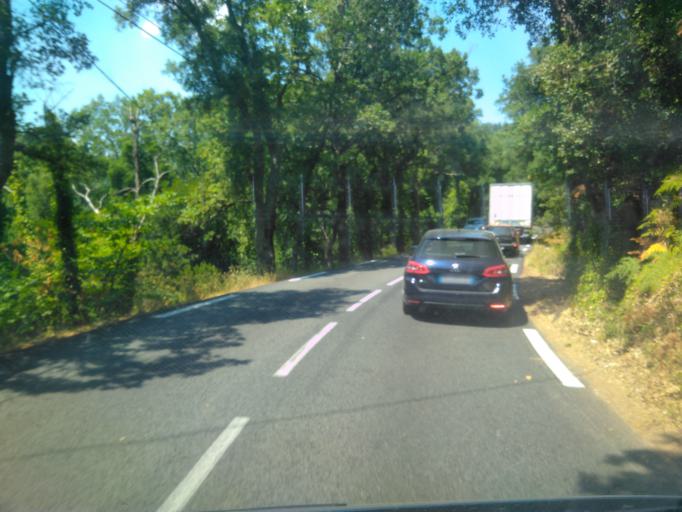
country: FR
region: Provence-Alpes-Cote d'Azur
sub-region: Departement du Var
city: La Garde-Freinet
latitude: 43.3274
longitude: 6.4711
